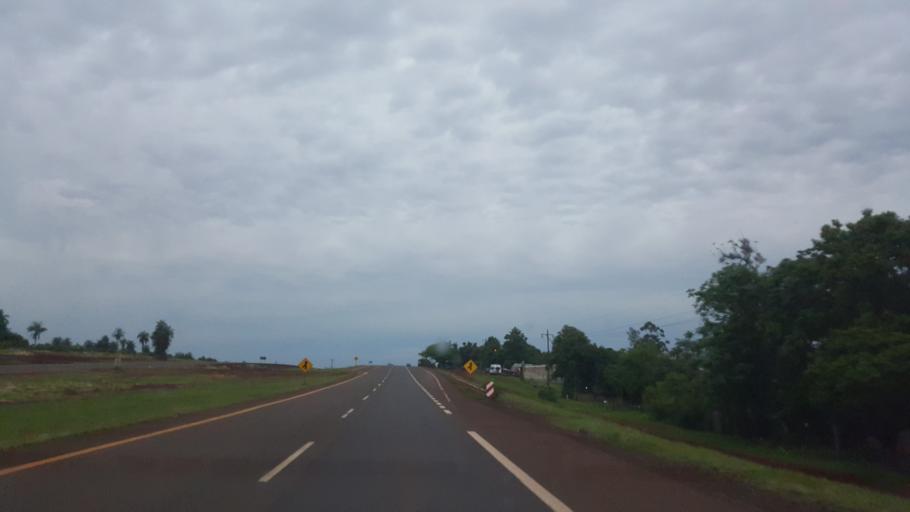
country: AR
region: Misiones
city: Garupa
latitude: -27.5378
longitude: -55.8541
